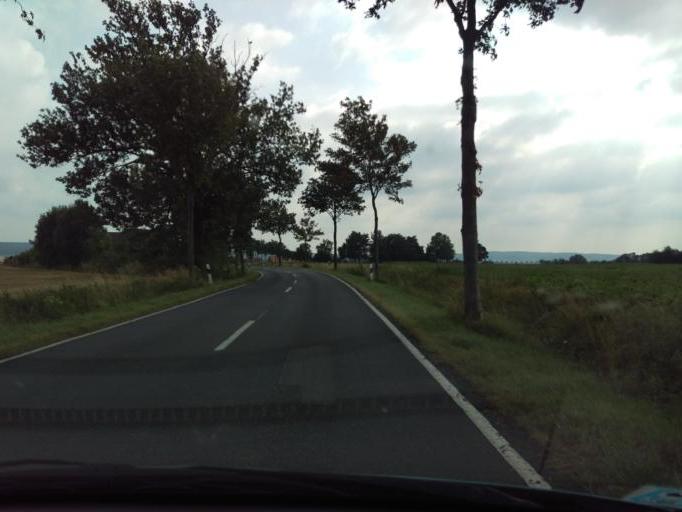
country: DE
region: Lower Saxony
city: Schellerten
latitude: 52.1751
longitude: 10.0978
